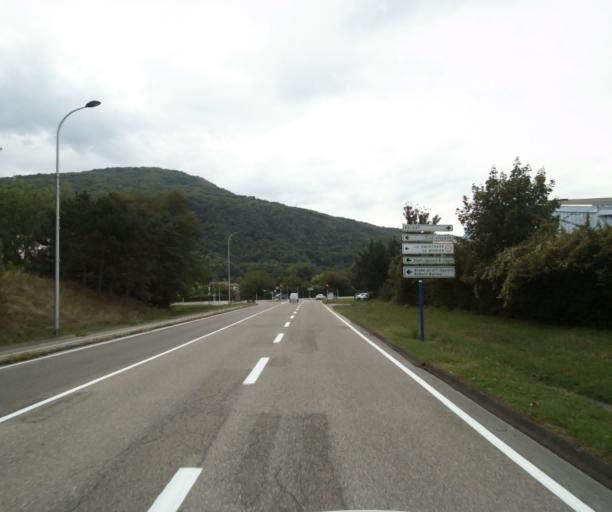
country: FR
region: Rhone-Alpes
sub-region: Departement de l'Isere
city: Saint-Martin-d'Heres
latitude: 45.1627
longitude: 5.7618
